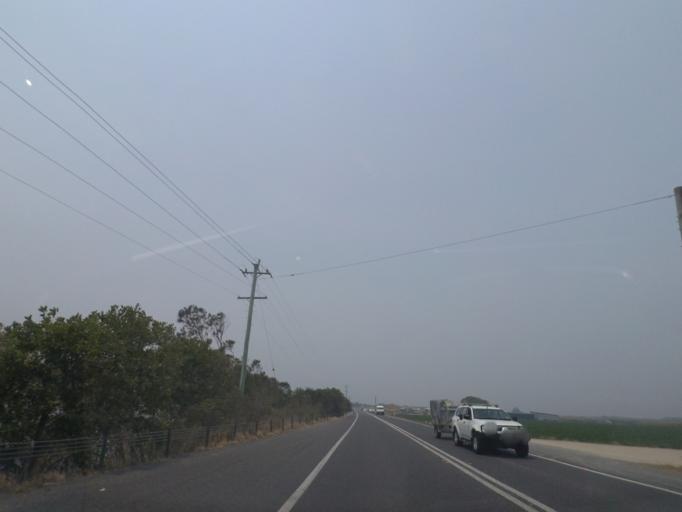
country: AU
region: New South Wales
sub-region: Richmond Valley
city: Evans Head
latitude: -28.9957
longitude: 153.4554
